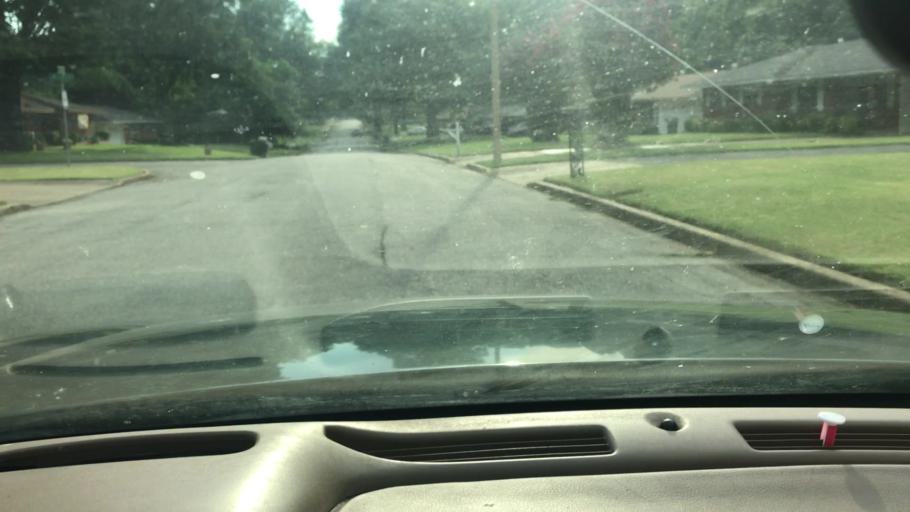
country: US
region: Mississippi
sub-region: De Soto County
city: Southaven
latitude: 35.0466
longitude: -90.0110
